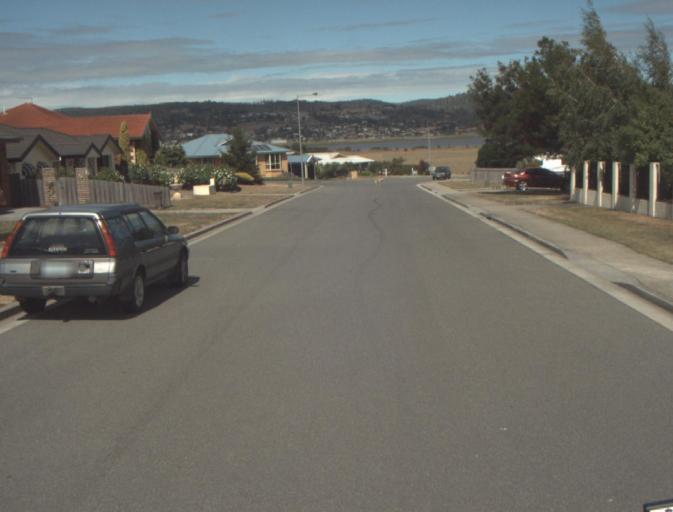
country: AU
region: Tasmania
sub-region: Launceston
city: Mayfield
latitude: -41.3876
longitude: 147.1094
